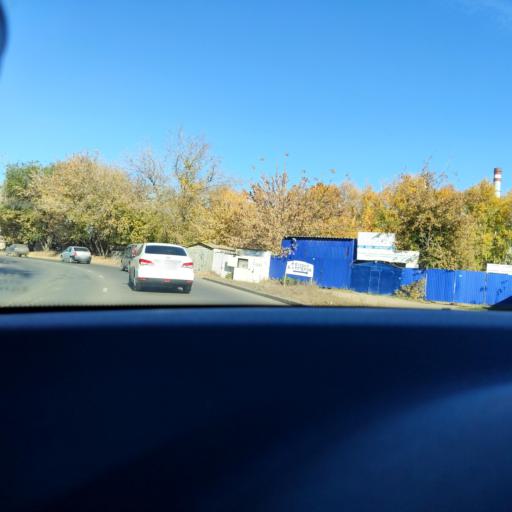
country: RU
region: Samara
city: Petra-Dubrava
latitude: 53.2430
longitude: 50.2727
